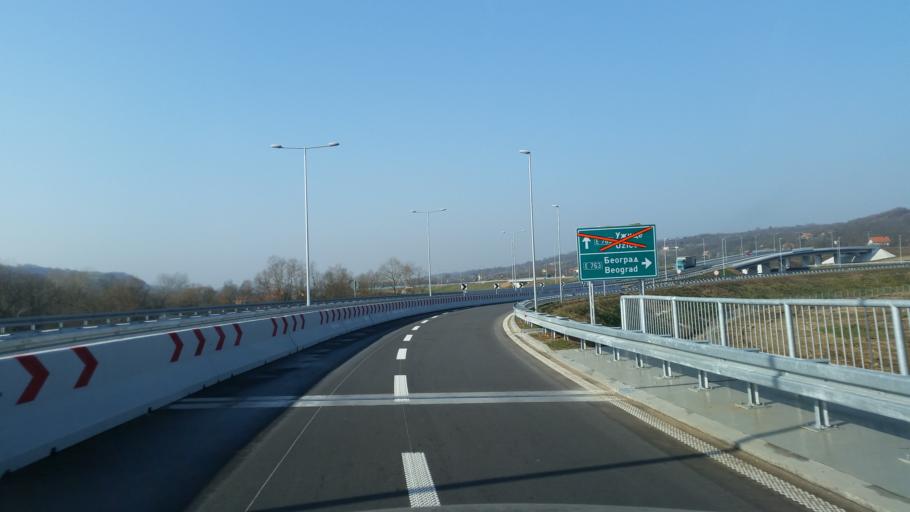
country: RS
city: Prislonica
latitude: 43.9176
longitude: 20.3970
